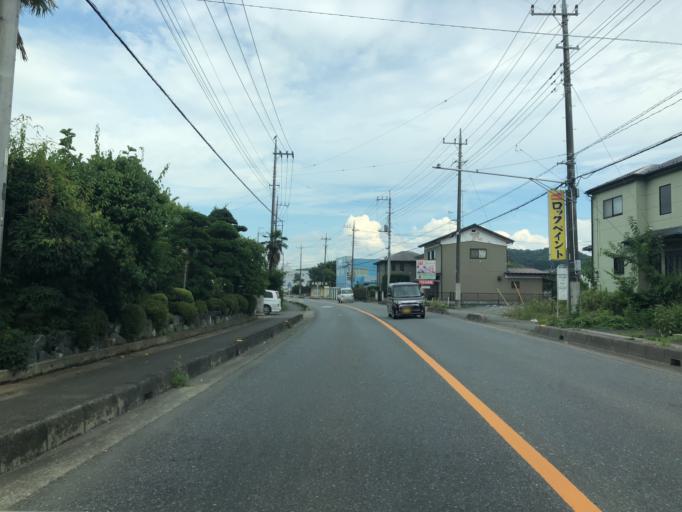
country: JP
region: Saitama
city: Fukiage-fujimi
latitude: 36.0606
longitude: 139.4099
